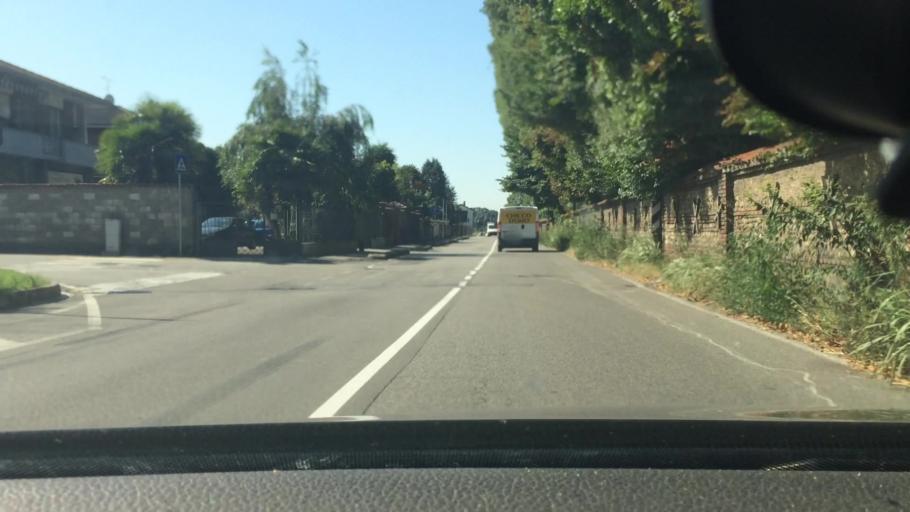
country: IT
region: Lombardy
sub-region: Citta metropolitana di Milano
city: Casorezzo
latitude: 45.5235
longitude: 8.9057
